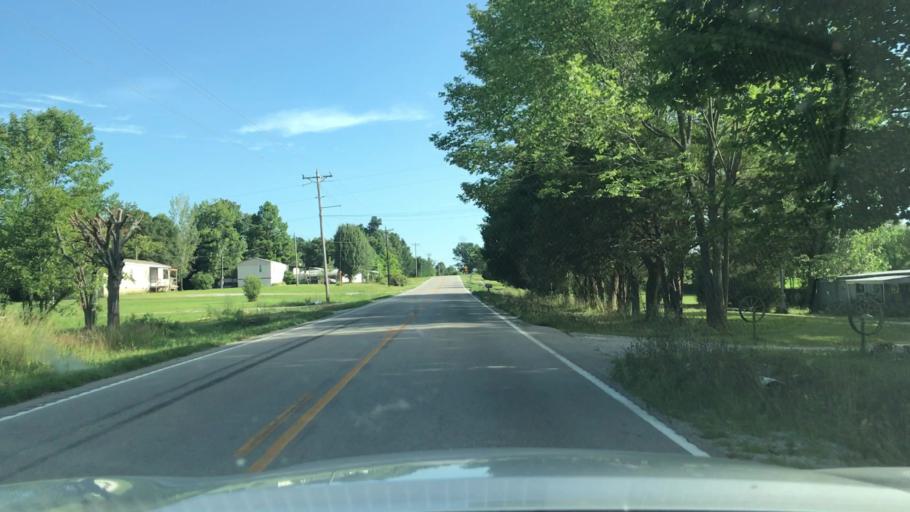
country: US
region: Kentucky
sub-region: Todd County
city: Elkton
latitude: 36.9260
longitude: -87.1624
